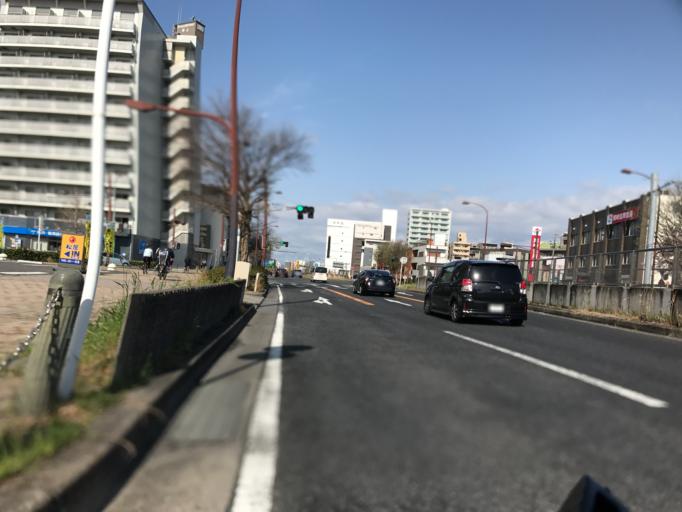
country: JP
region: Aichi
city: Nagoya-shi
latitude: 35.1592
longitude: 136.9391
